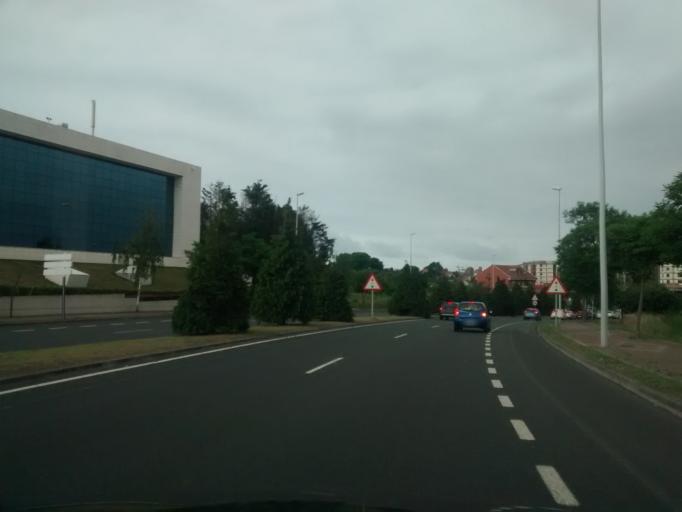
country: ES
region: Cantabria
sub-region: Provincia de Cantabria
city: Santander
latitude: 43.4666
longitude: -3.8337
